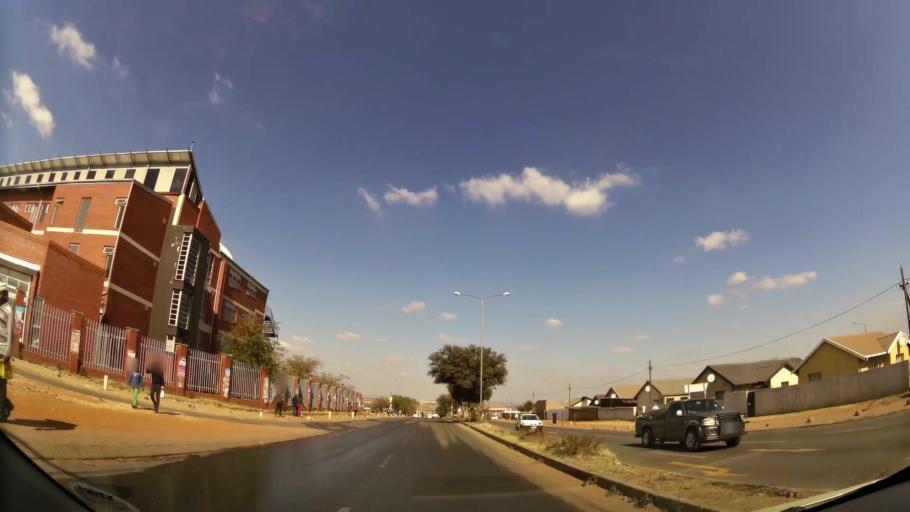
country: ZA
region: Gauteng
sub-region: West Rand District Municipality
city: Krugersdorp
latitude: -26.1636
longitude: 27.7801
